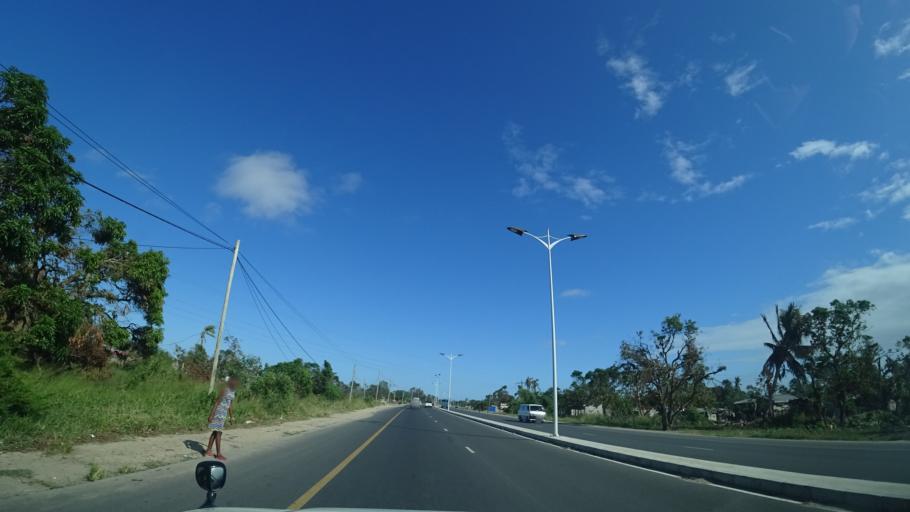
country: MZ
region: Sofala
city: Beira
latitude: -19.7361
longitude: 34.8355
